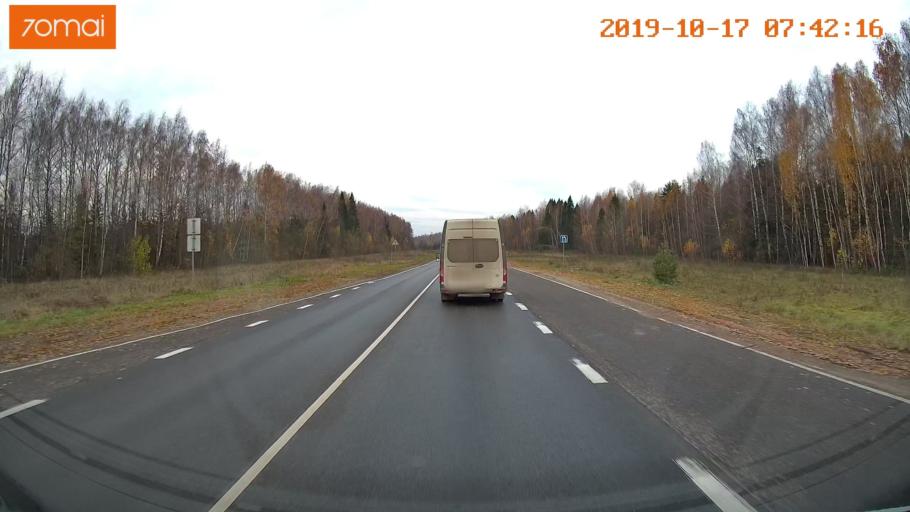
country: RU
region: Vladimir
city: Yur'yev-Pol'skiy
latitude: 56.4841
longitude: 39.7908
